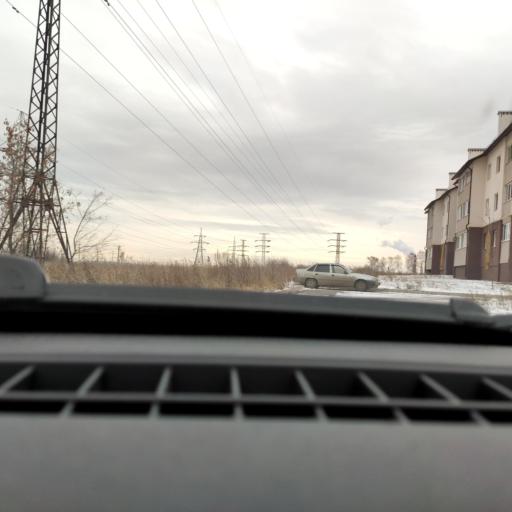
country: RU
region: Bashkortostan
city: Avdon
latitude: 54.6981
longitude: 55.8055
